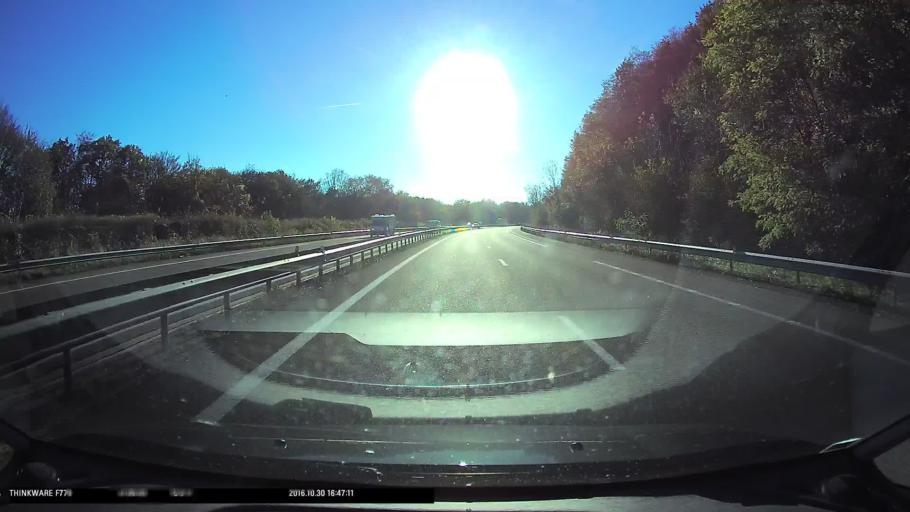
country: FR
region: Franche-Comte
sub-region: Departement du Doubs
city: Chatillon-le-Duc
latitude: 47.2883
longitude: 6.0119
